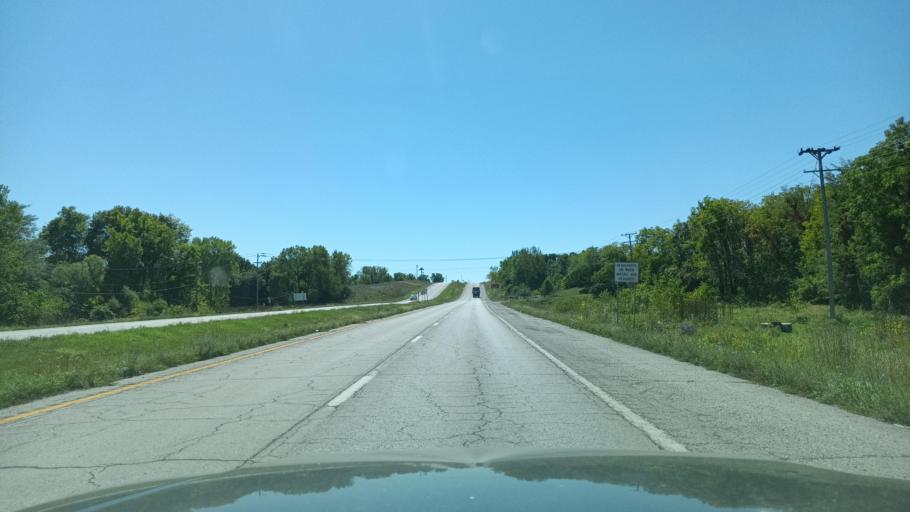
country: US
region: Missouri
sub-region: Adair County
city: Kirksville
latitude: 40.1657
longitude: -92.5722
